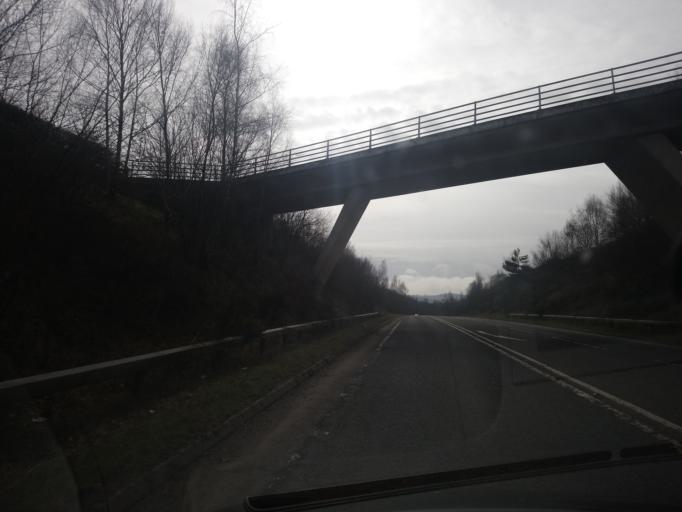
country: GB
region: England
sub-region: Telford and Wrekin
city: Ironbridge
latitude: 52.6483
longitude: -2.5086
